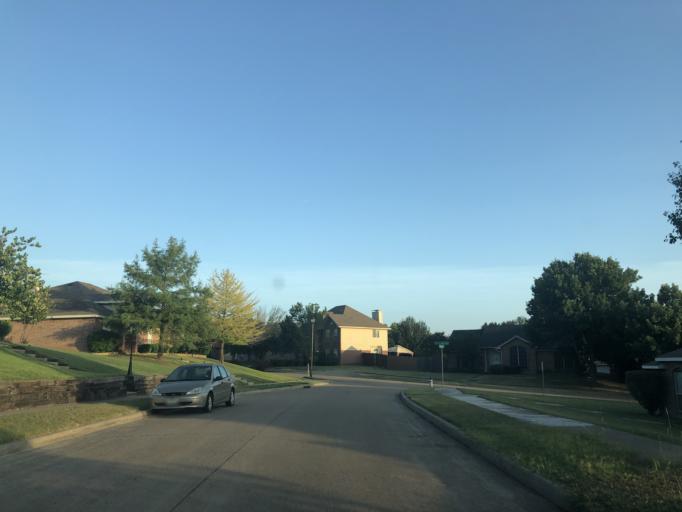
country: US
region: Texas
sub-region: Dallas County
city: Duncanville
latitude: 32.6474
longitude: -96.9532
